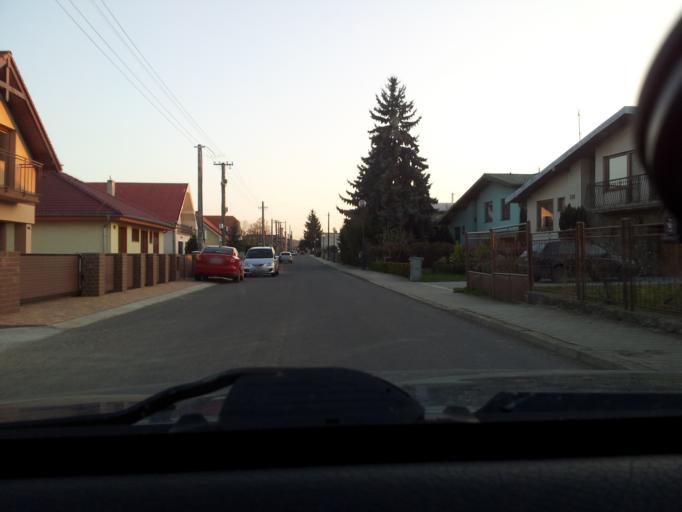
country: SK
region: Nitriansky
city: Tlmace
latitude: 48.3196
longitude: 18.5286
